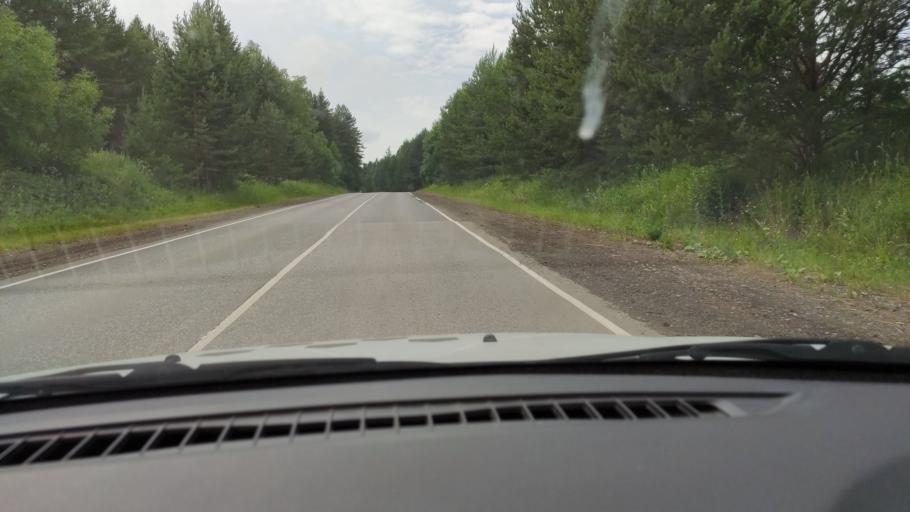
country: RU
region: Perm
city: Kukushtan
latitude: 57.4822
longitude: 56.5988
